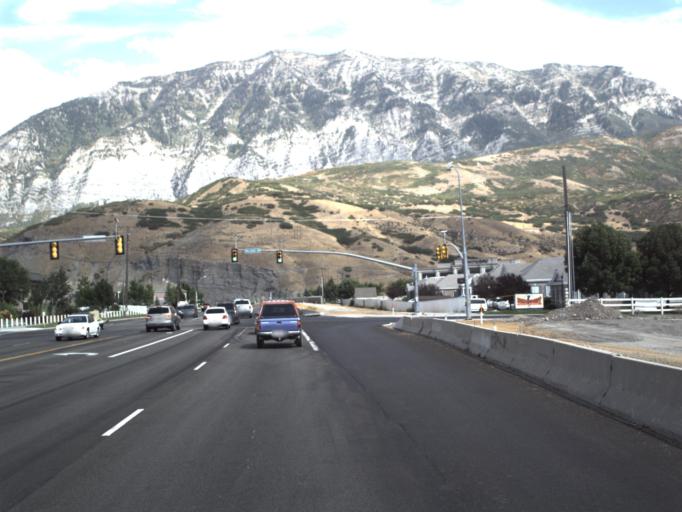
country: US
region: Utah
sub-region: Utah County
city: Orem
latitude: 40.3119
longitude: -111.6688
